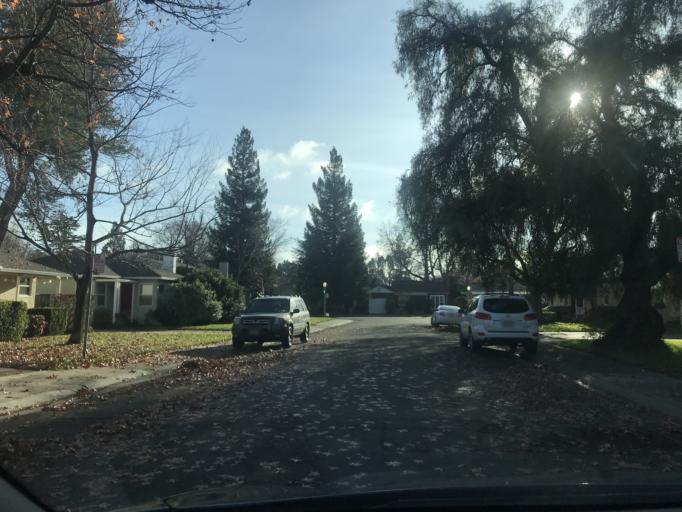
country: US
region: California
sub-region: Sacramento County
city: Sacramento
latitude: 38.5611
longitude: -121.4976
